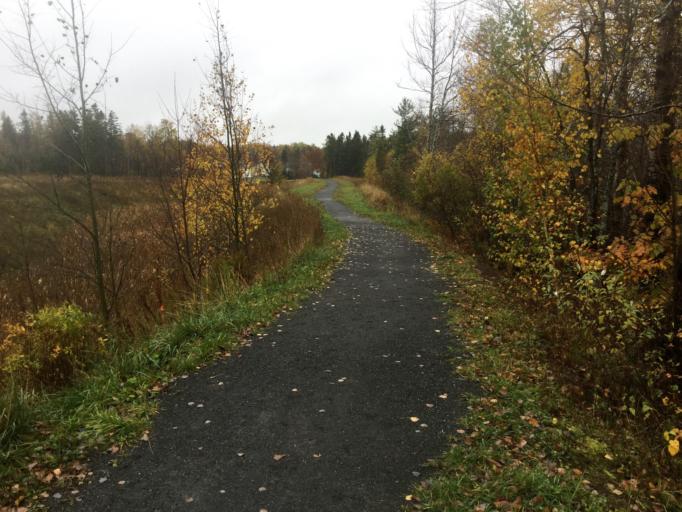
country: CA
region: Nova Scotia
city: New Glasgow
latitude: 45.5515
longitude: -62.6773
